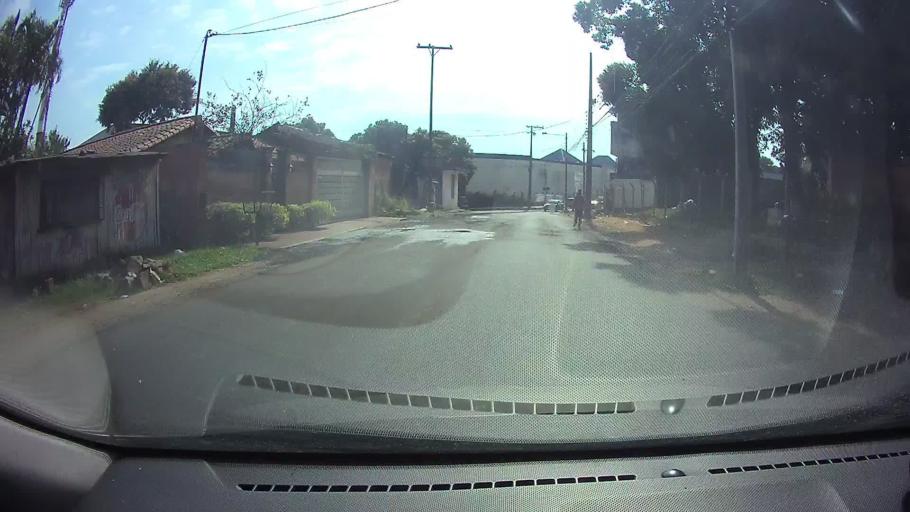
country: PY
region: Central
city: Fernando de la Mora
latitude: -25.3099
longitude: -57.5526
